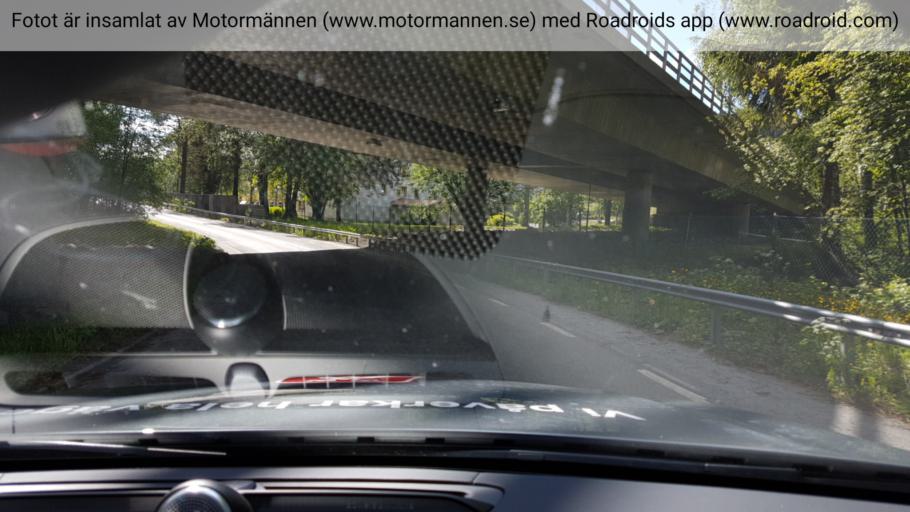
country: SE
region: Jaemtland
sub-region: OEstersunds Kommun
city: Ostersund
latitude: 63.1828
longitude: 14.6278
